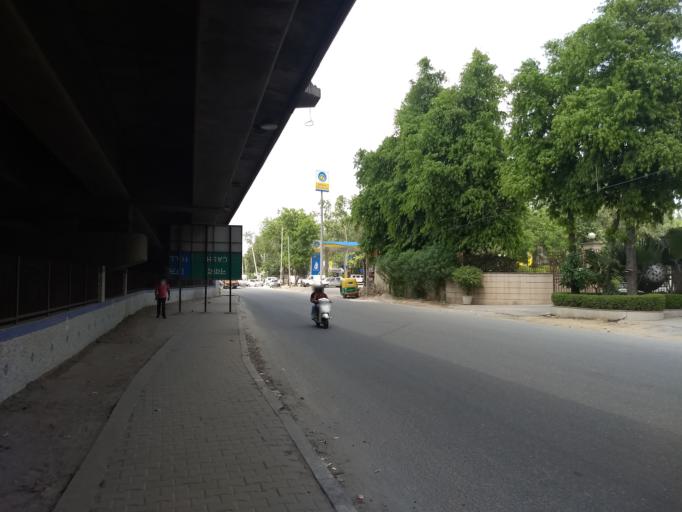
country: IN
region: Haryana
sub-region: Gurgaon
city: Gurgaon
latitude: 28.5224
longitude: 77.0991
